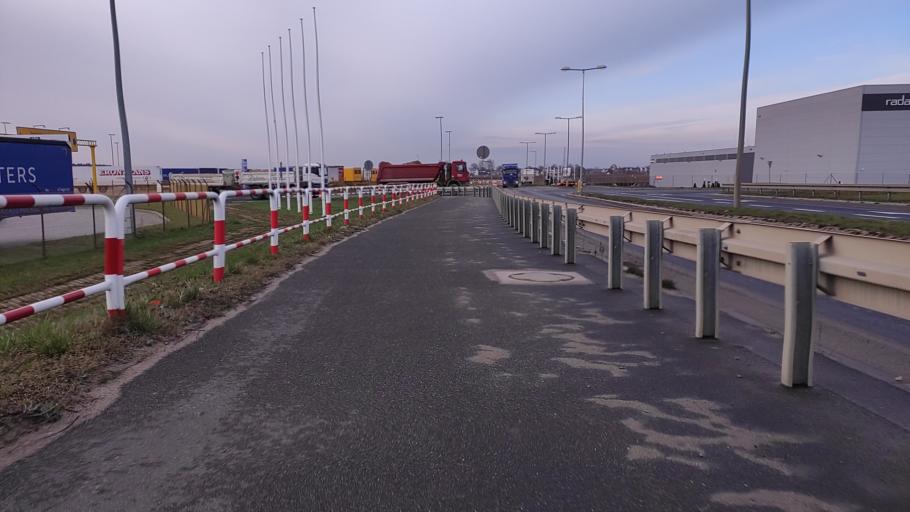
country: PL
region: Greater Poland Voivodeship
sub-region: Powiat poznanski
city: Swarzedz
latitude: 52.3991
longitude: 17.1219
